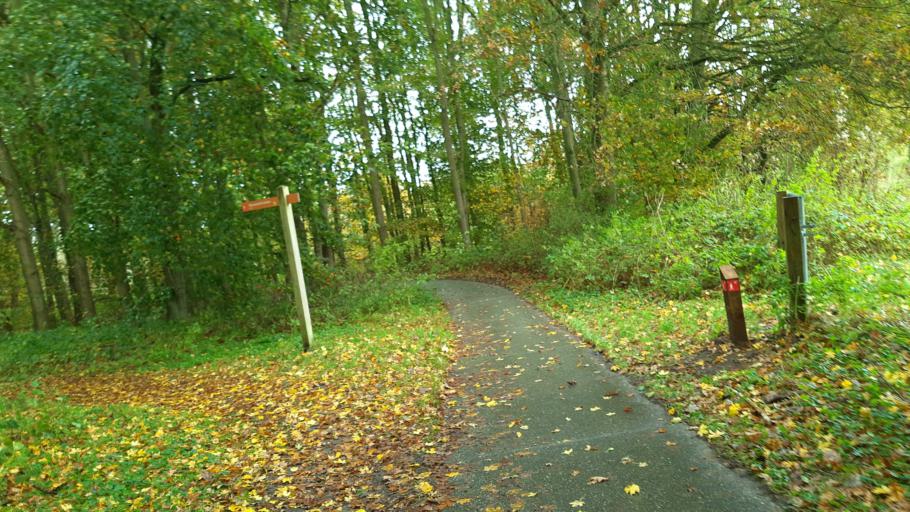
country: NL
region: Friesland
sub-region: Gemeente Lemsterland
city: Echtenerbrug
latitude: 52.7898
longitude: 5.7943
